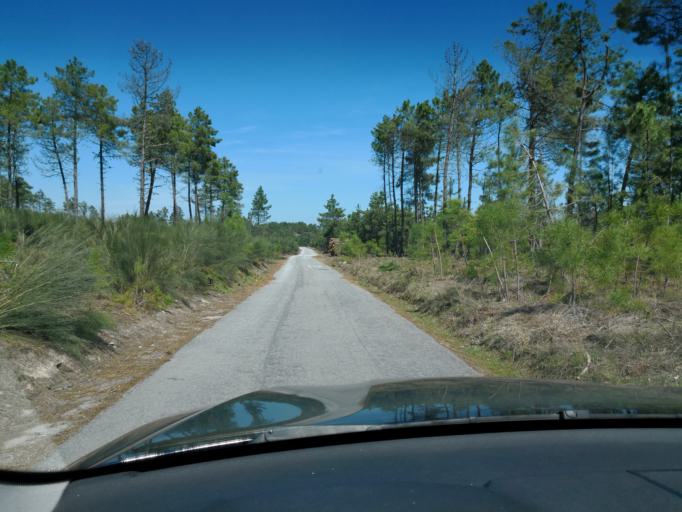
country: PT
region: Vila Real
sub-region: Vila Real
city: Vila Real
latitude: 41.3270
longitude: -7.6543
